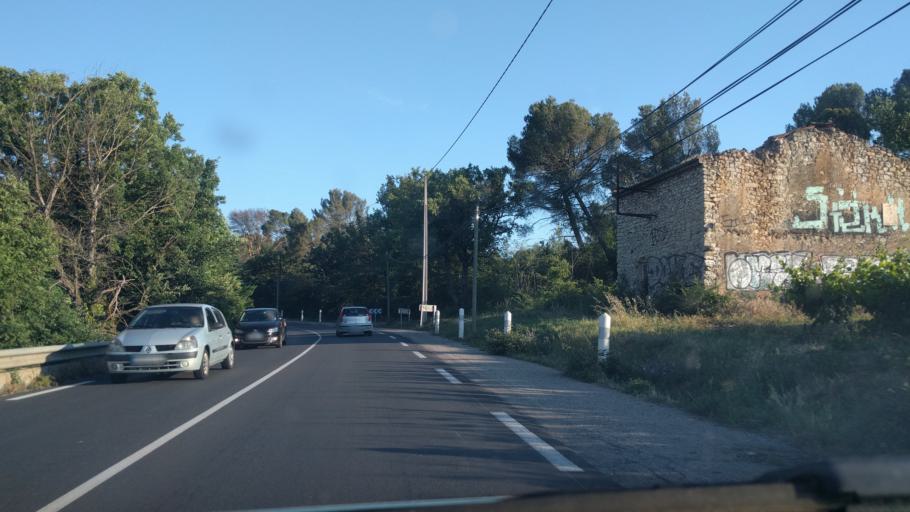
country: FR
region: Provence-Alpes-Cote d'Azur
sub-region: Departement des Bouches-du-Rhone
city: Venelles
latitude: 43.6234
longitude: 5.4903
